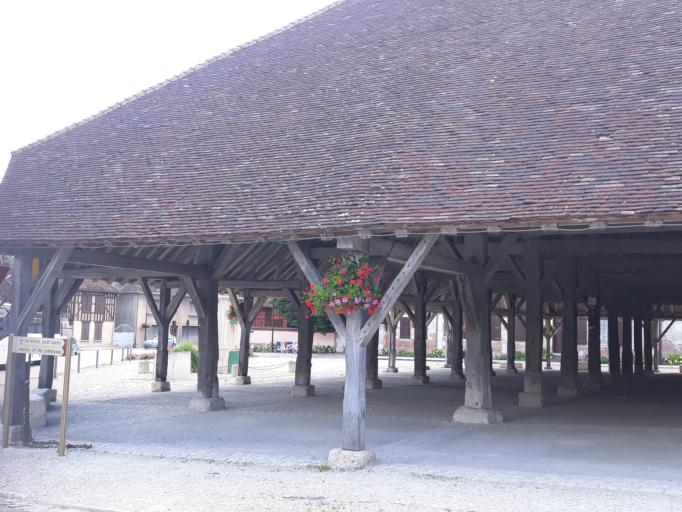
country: FR
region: Champagne-Ardenne
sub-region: Departement de l'Aube
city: Piney
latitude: 48.3636
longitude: 4.3329
